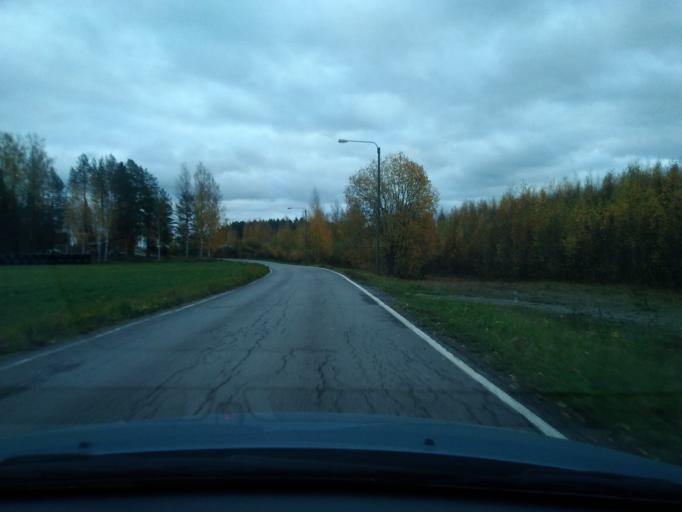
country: FI
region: Central Finland
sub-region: Saarijaervi-Viitasaari
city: Saarijaervi
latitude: 62.6889
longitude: 25.3169
